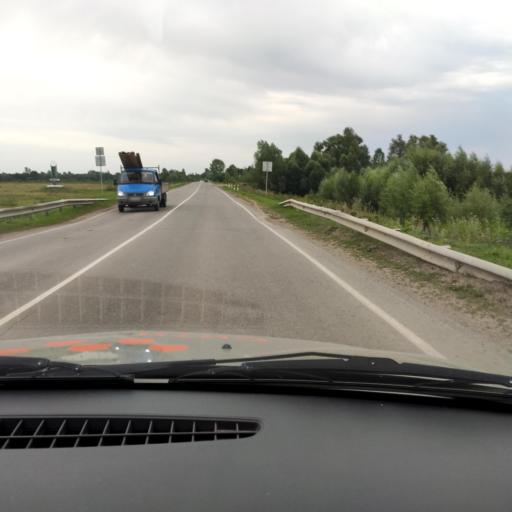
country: RU
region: Bashkortostan
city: Krasnaya Gorka
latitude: 55.1756
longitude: 56.6667
